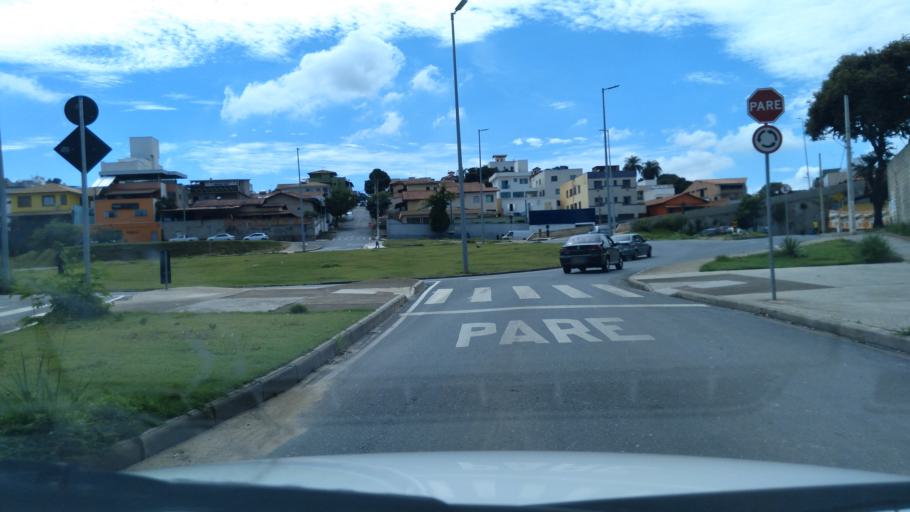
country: BR
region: Minas Gerais
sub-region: Belo Horizonte
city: Belo Horizonte
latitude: -19.8746
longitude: -43.9193
